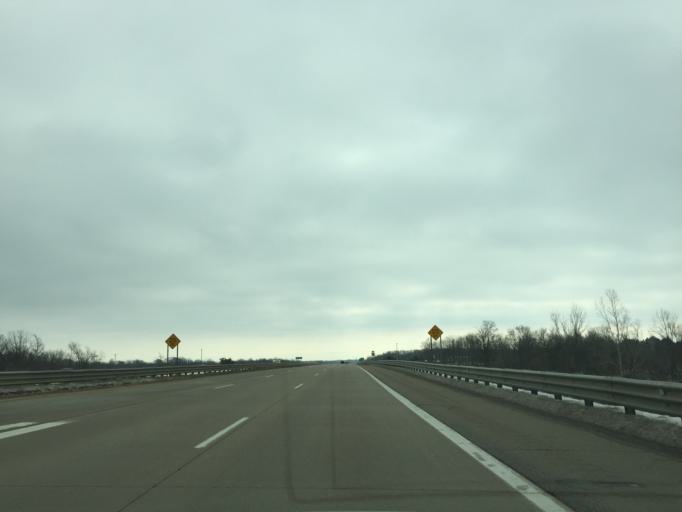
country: US
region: Michigan
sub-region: Ottawa County
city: Hudsonville
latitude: 42.8583
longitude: -85.8155
